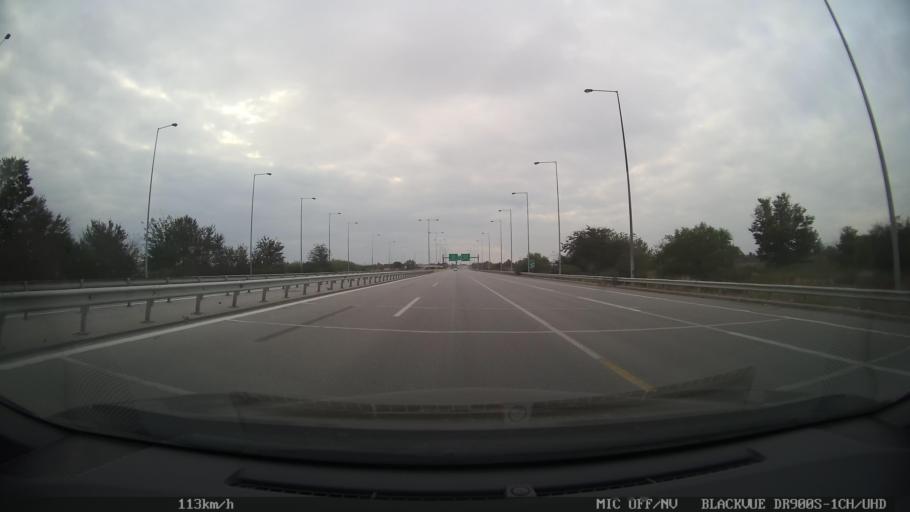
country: GR
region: Central Macedonia
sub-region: Nomos Thessalonikis
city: Kalochori
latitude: 40.6602
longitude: 22.8391
